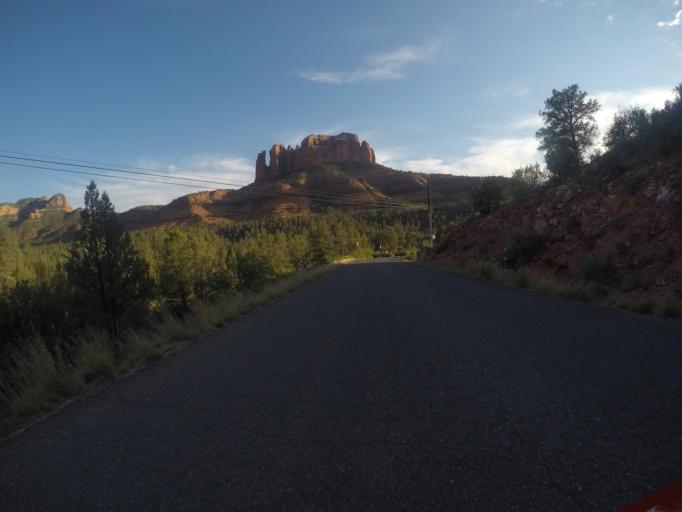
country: US
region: Arizona
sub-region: Yavapai County
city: West Sedona
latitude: 34.8258
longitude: -111.7874
